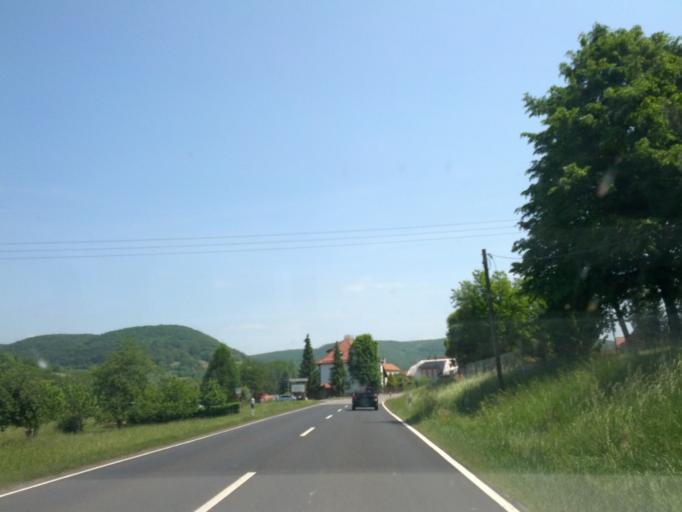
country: DE
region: Thuringia
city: Klings
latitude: 50.6634
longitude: 10.1221
